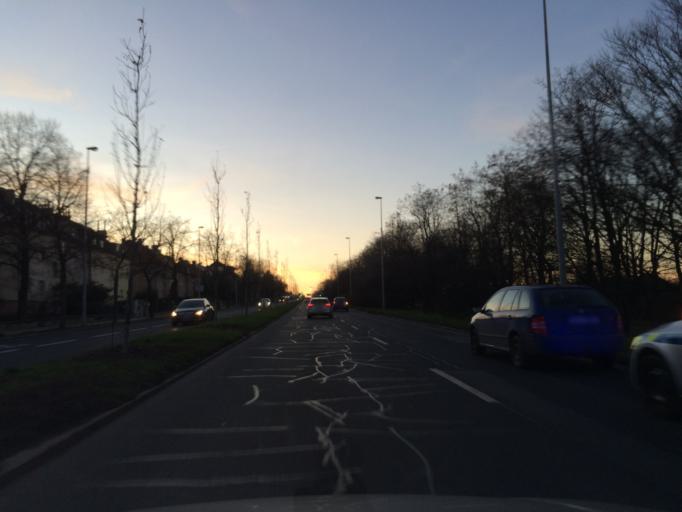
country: CZ
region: Central Bohemia
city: Horomerice
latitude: 50.0929
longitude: 14.3193
